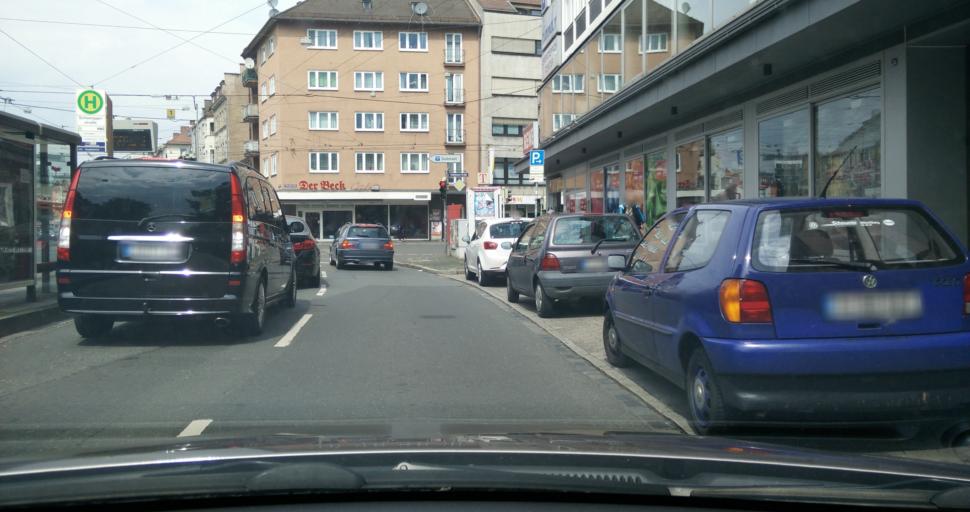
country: DE
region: Bavaria
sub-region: Regierungsbezirk Mittelfranken
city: Nuernberg
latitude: 49.4411
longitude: 11.0903
